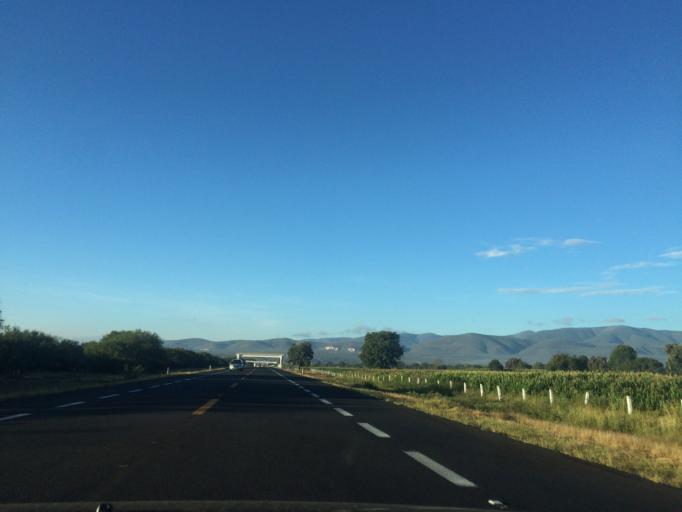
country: MX
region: Puebla
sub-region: Santiago Miahuatlan
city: San Jose Monte Chiquito
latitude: 18.5126
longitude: -97.4544
